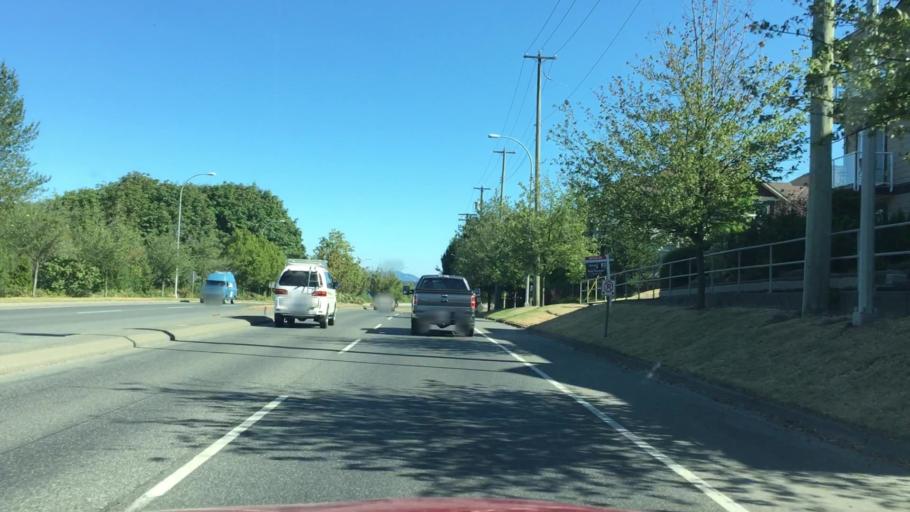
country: CA
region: British Columbia
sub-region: Cowichan Valley Regional District
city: Ladysmith
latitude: 48.9924
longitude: -123.8135
